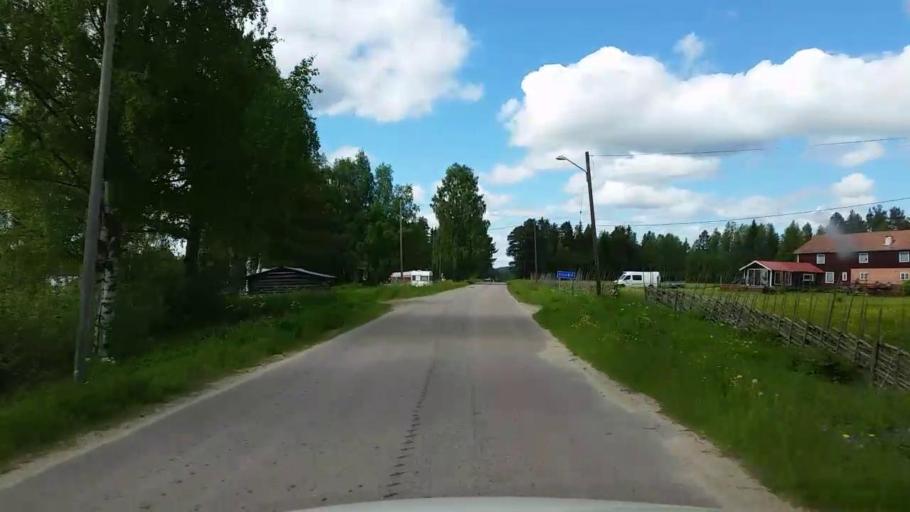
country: SE
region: Gaevleborg
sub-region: Ovanakers Kommun
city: Alfta
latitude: 61.4812
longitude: 15.9939
